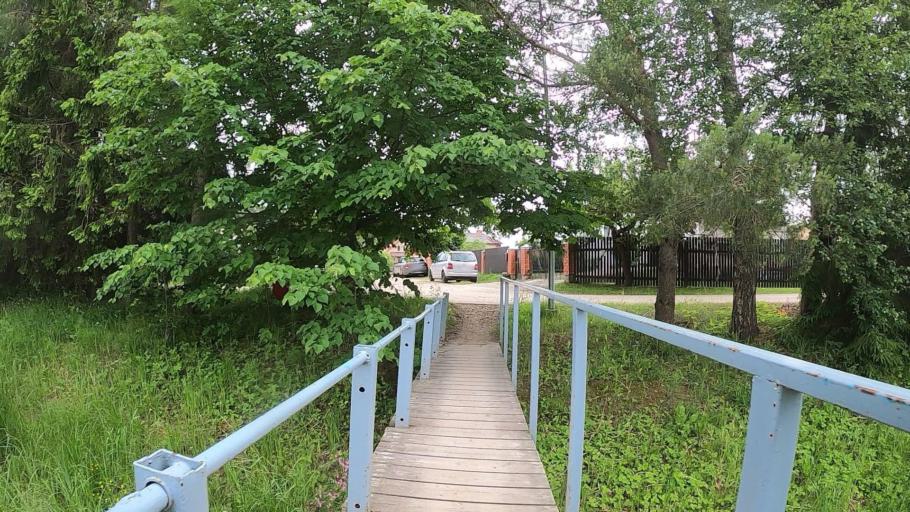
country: LV
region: Ozolnieku
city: Ozolnieki
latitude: 56.6914
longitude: 23.7679
